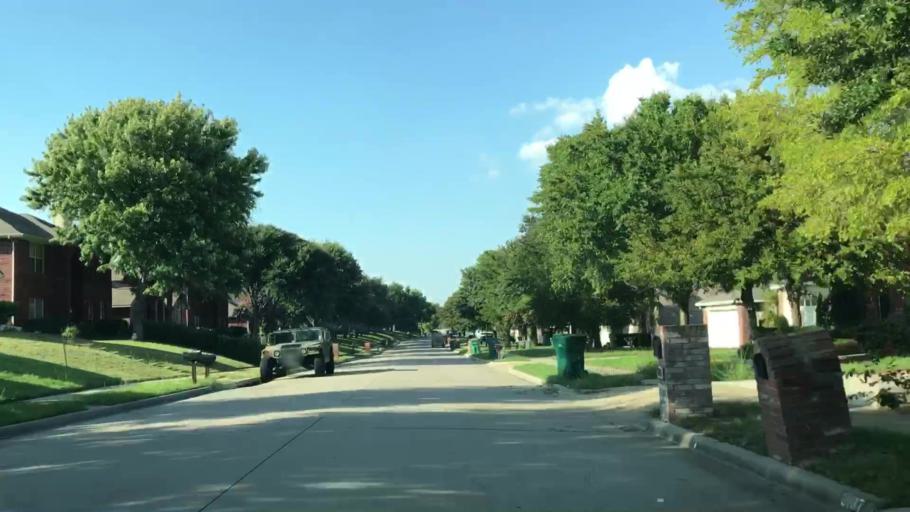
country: US
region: Texas
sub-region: Denton County
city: Lewisville
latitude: 33.0083
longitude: -97.0113
